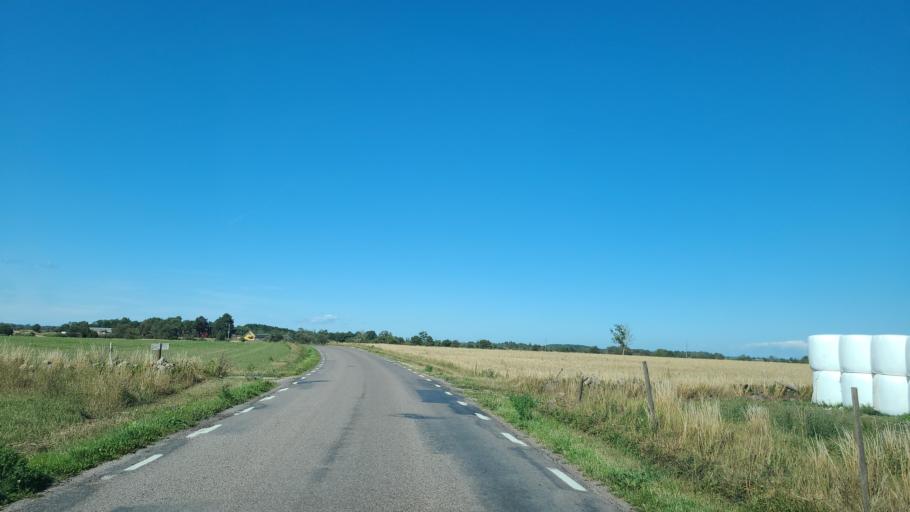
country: SE
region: Kalmar
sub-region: Borgholms Kommun
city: Borgholm
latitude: 56.8616
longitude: 16.8189
